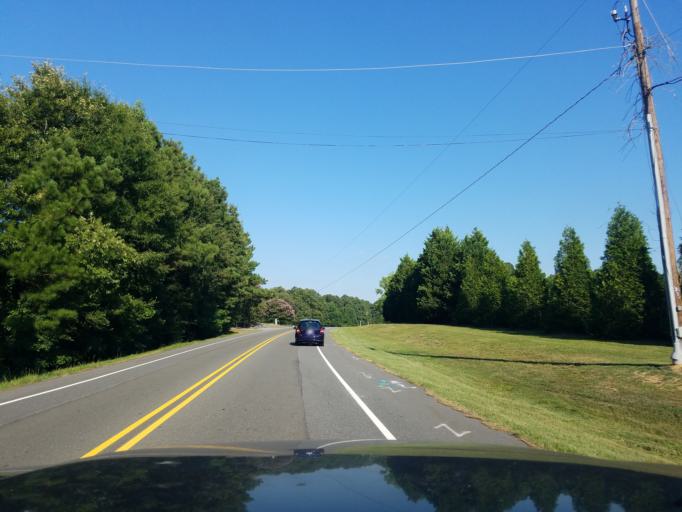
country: US
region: North Carolina
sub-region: Orange County
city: Chapel Hill
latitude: 35.8867
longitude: -78.9773
